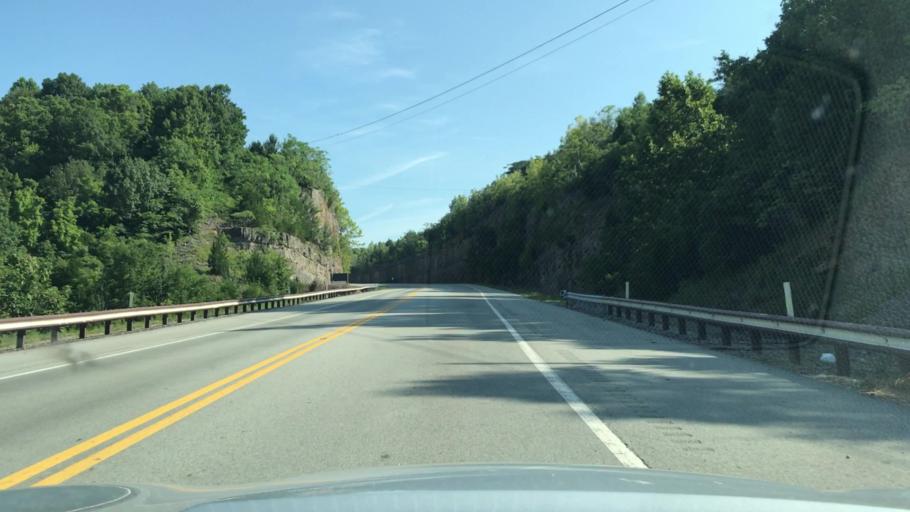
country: US
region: Tennessee
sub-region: Pickett County
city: Byrdstown
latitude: 36.5358
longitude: -85.1602
